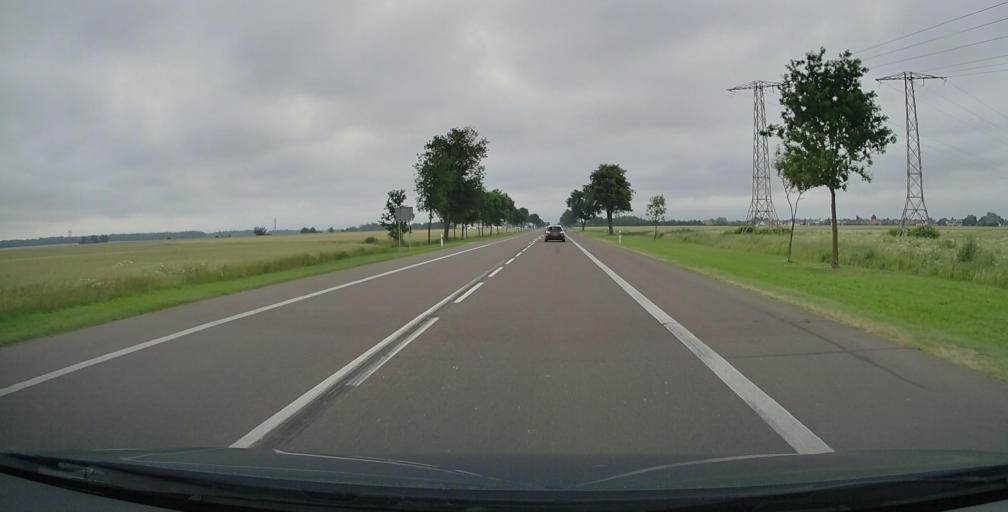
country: PL
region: Lublin Voivodeship
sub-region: Powiat bialski
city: Miedzyrzec Podlaski
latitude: 52.0000
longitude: 22.7872
